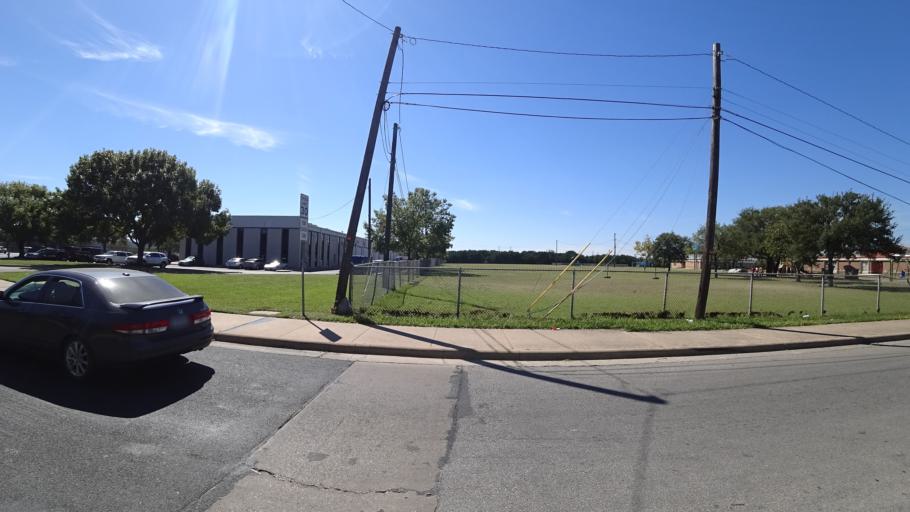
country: US
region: Texas
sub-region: Travis County
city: Austin
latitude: 30.2785
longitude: -97.6721
